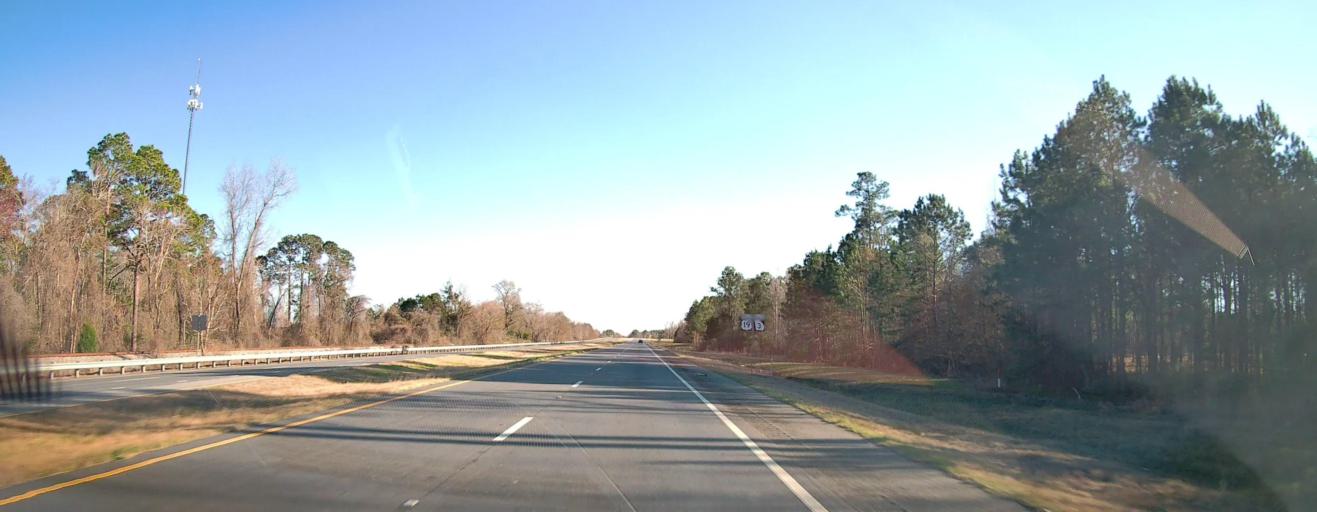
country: US
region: Georgia
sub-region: Lee County
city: Leesburg
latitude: 31.8299
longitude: -84.2186
